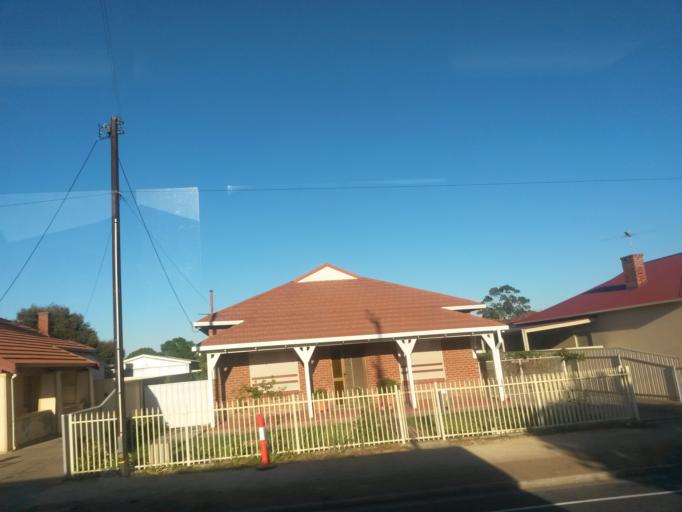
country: AU
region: South Australia
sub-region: Port Adelaide Enfield
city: Alberton
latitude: -34.8529
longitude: 138.5290
